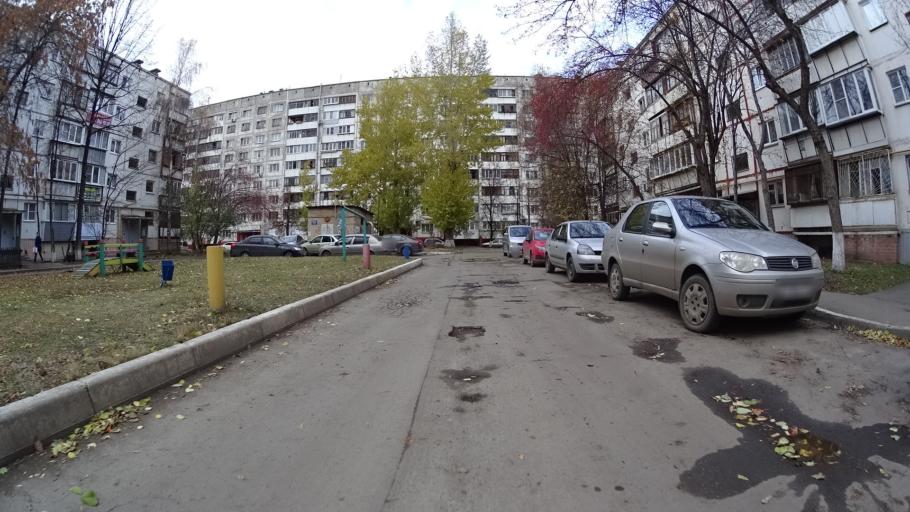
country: RU
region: Chelyabinsk
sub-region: Gorod Chelyabinsk
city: Chelyabinsk
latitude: 55.1932
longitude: 61.3133
